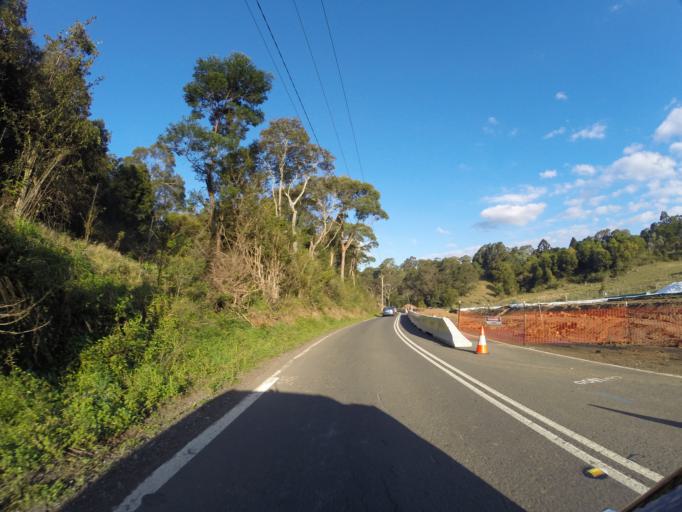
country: AU
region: New South Wales
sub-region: Wollongong
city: Cordeaux Heights
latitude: -34.4328
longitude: 150.8307
